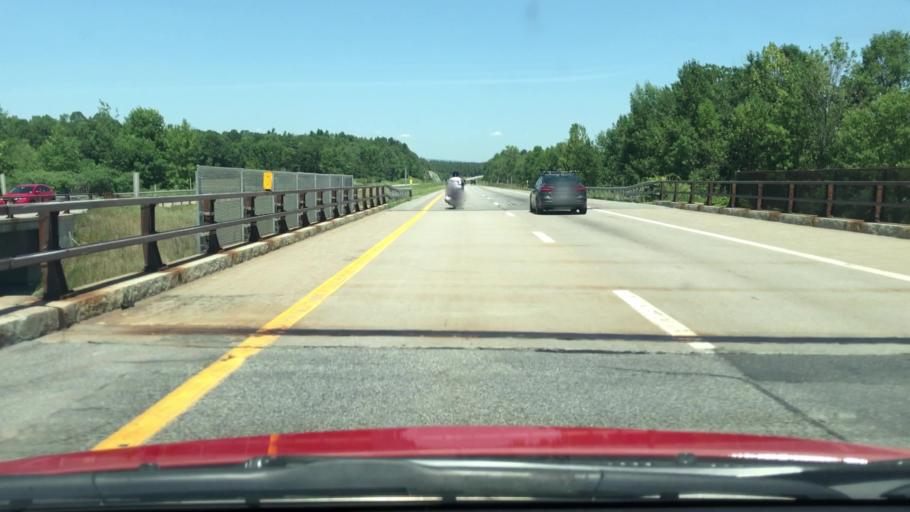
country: US
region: New York
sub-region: Essex County
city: Keeseville
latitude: 44.4666
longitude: -73.4855
